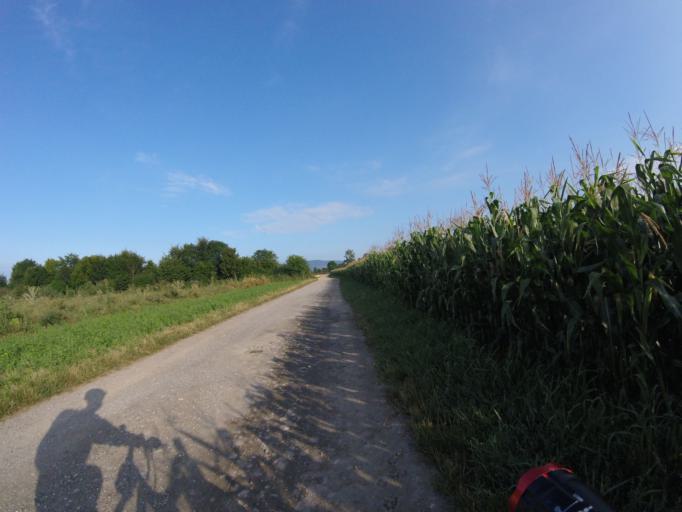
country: AT
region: Lower Austria
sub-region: Politischer Bezirk Baden
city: Trumau
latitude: 48.0025
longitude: 16.3662
